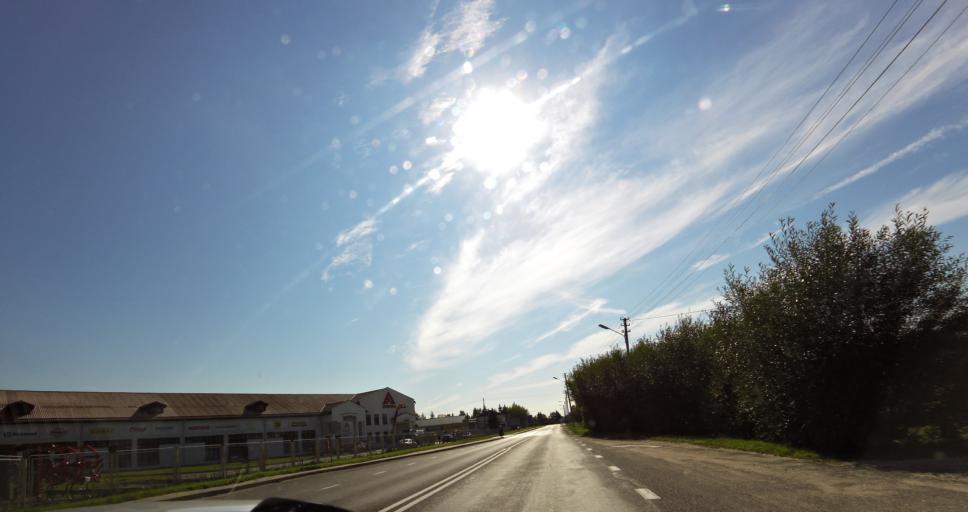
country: LT
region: Panevezys
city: Pasvalys
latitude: 56.0690
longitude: 24.3847
